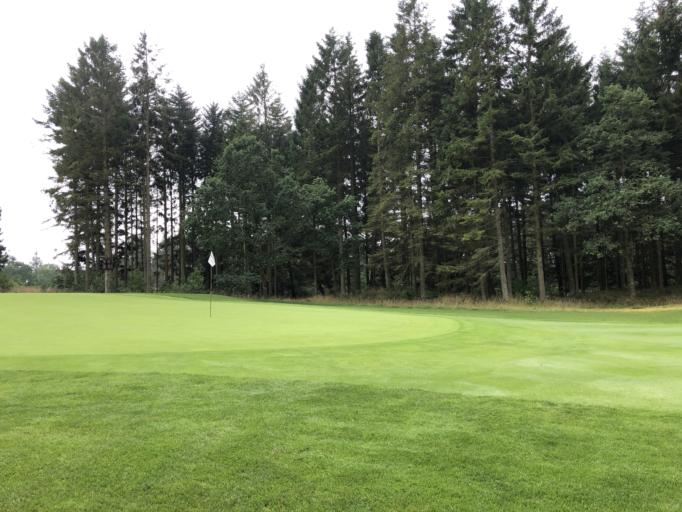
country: DK
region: Central Jutland
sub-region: Holstebro Kommune
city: Ulfborg
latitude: 56.3241
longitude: 8.4323
